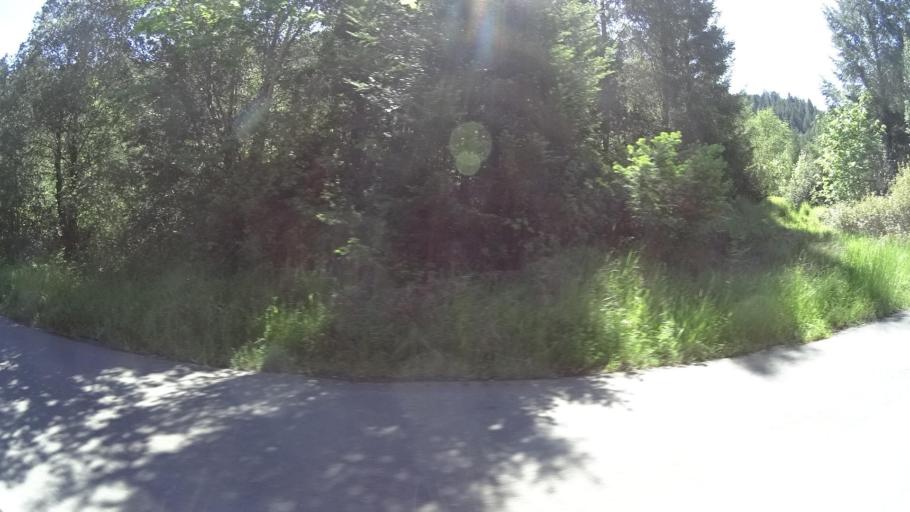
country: US
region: California
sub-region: Humboldt County
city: Rio Dell
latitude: 40.2295
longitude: -124.1104
